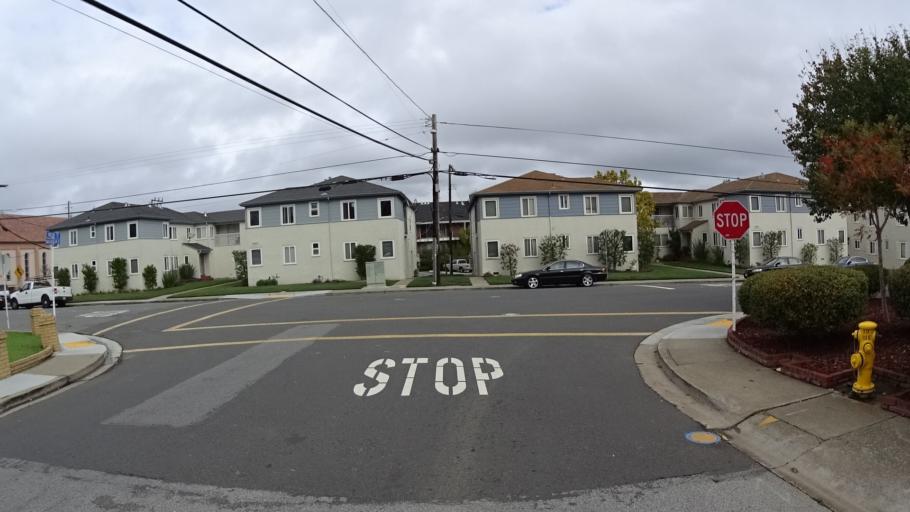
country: US
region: California
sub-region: San Mateo County
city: Millbrae
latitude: 37.6053
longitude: -122.3991
